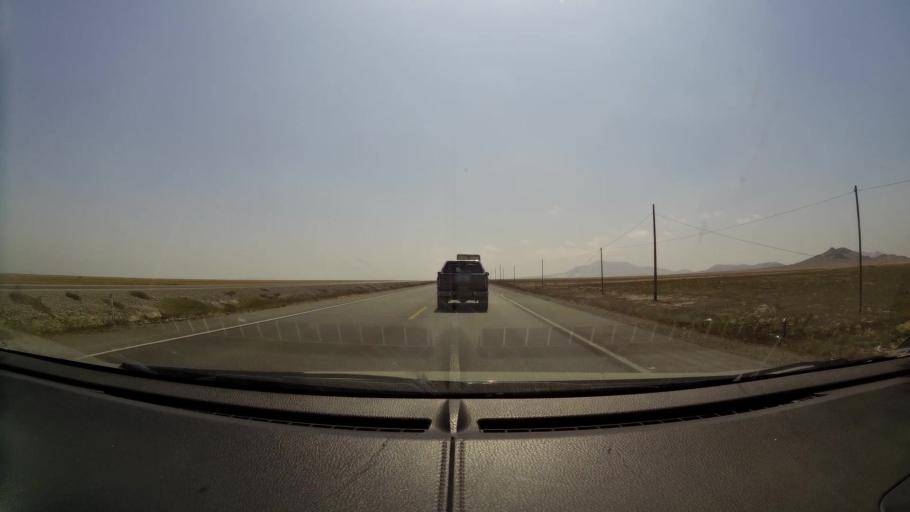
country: PE
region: Lambayeque
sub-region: Provincia de Chiclayo
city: Mocupe
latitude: -6.9573
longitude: -79.6935
